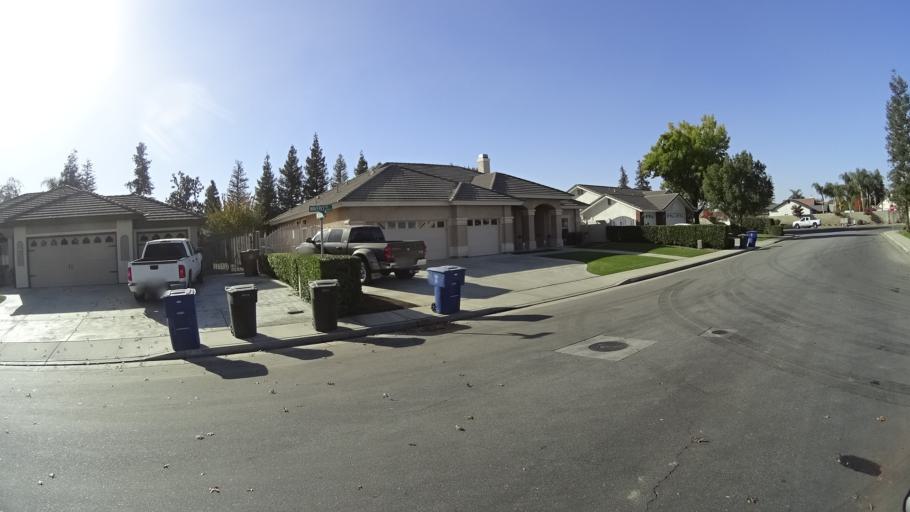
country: US
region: California
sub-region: Kern County
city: Greenfield
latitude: 35.2801
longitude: -119.0470
